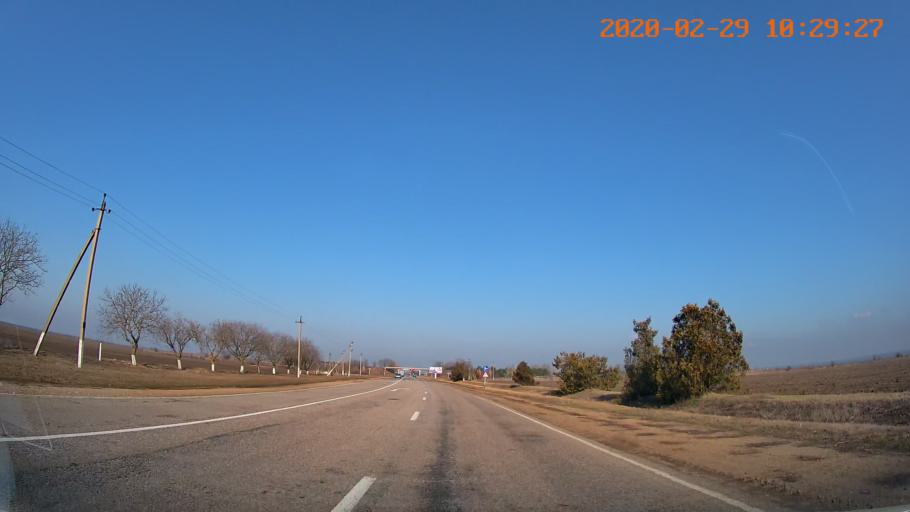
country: MD
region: Telenesti
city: Tiraspolul Nou
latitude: 46.9237
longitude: 29.5856
